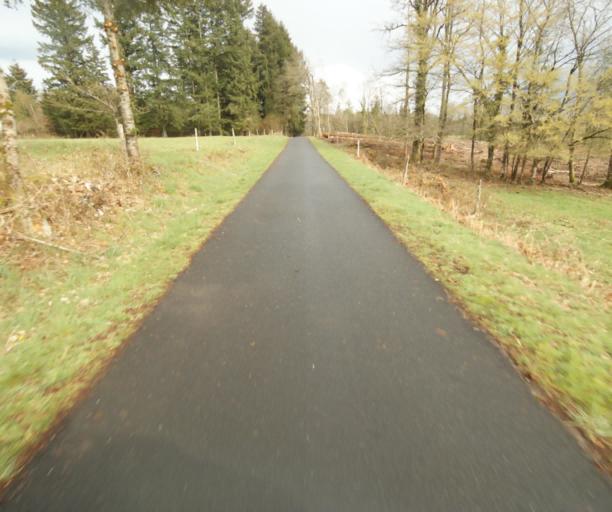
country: FR
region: Limousin
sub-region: Departement de la Correze
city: Saint-Privat
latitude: 45.2315
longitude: 1.9990
